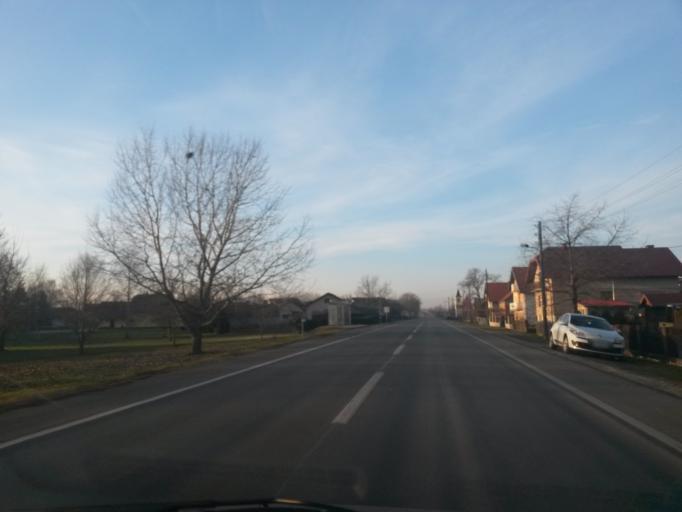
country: HR
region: Varazdinska
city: Jalzabet
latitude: 46.2896
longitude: 16.5007
